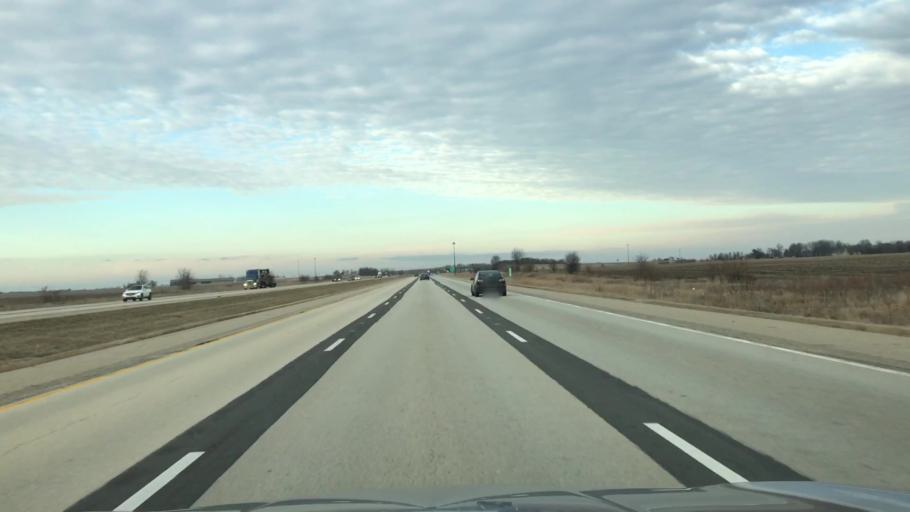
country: US
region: Illinois
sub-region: Sangamon County
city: Williamsville
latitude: 40.0100
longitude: -89.5000
